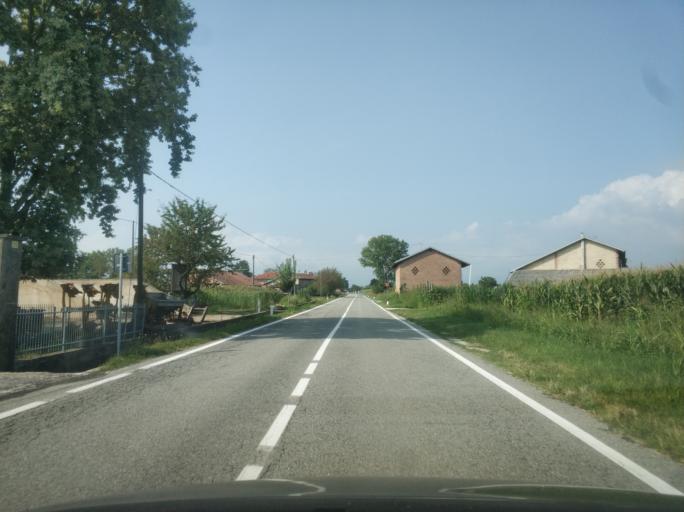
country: IT
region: Piedmont
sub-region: Provincia di Cuneo
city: Tarantasca
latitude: 44.4912
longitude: 7.5539
